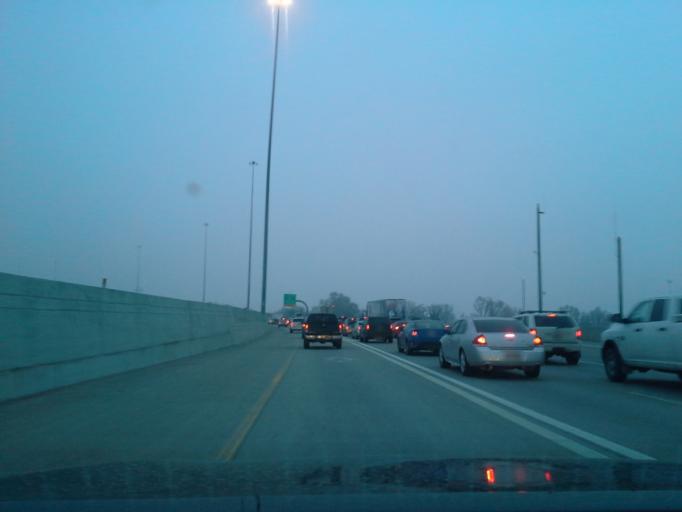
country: US
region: Utah
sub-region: Salt Lake County
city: Midvale
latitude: 40.6375
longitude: -111.9044
